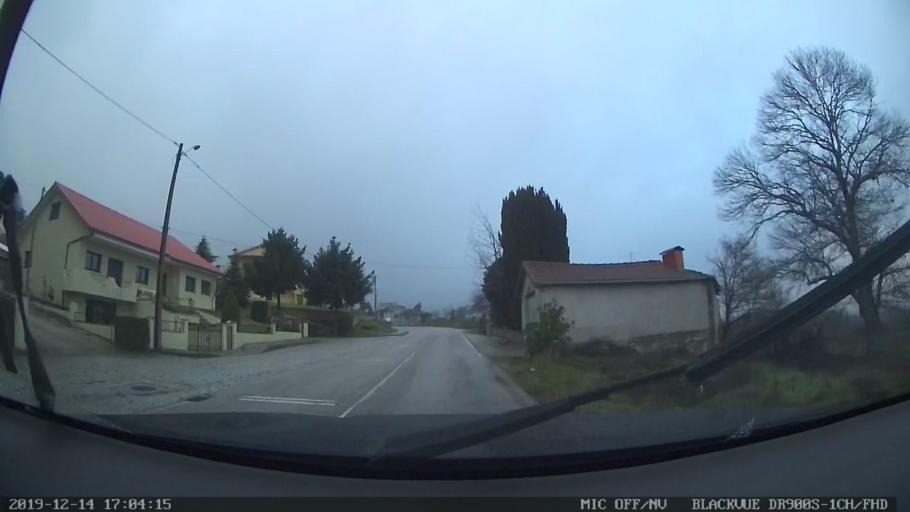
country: PT
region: Vila Real
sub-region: Vila Pouca de Aguiar
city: Vila Pouca de Aguiar
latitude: 41.4466
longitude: -7.5730
